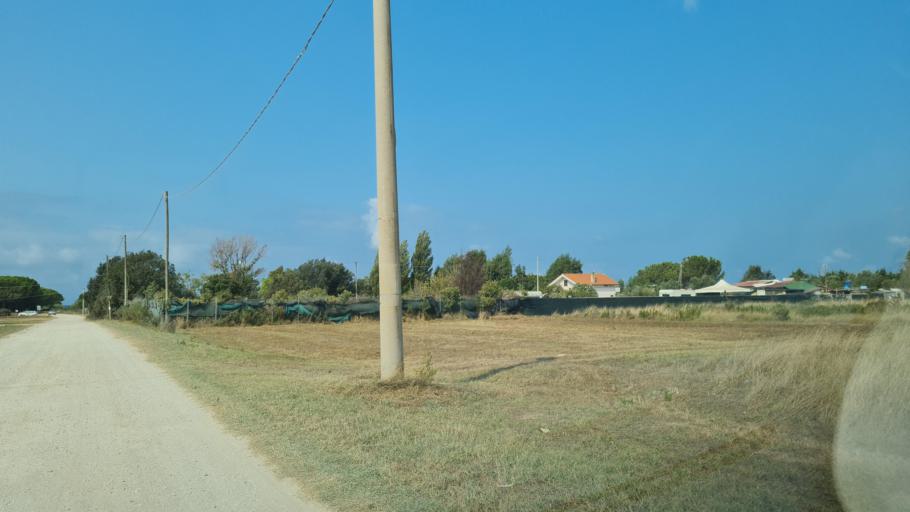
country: IT
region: Latium
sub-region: Provincia di Viterbo
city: Tarquinia
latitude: 42.1917
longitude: 11.7279
